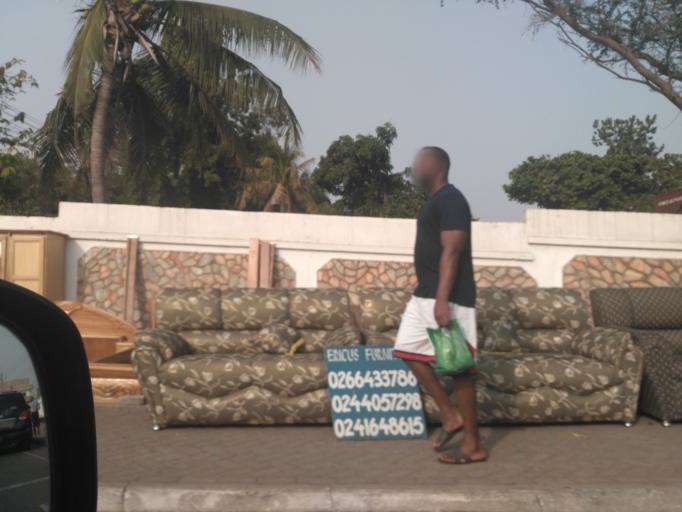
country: GH
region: Greater Accra
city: Accra
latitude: 5.5747
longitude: -0.2008
